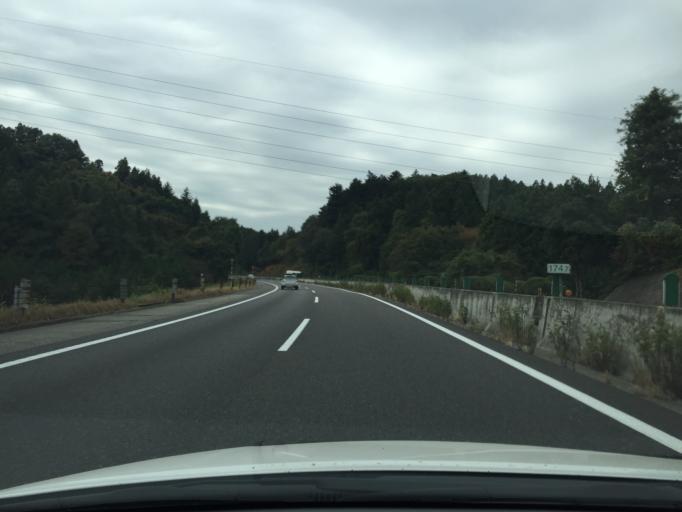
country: JP
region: Fukushima
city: Sukagawa
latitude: 37.1473
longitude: 140.2035
